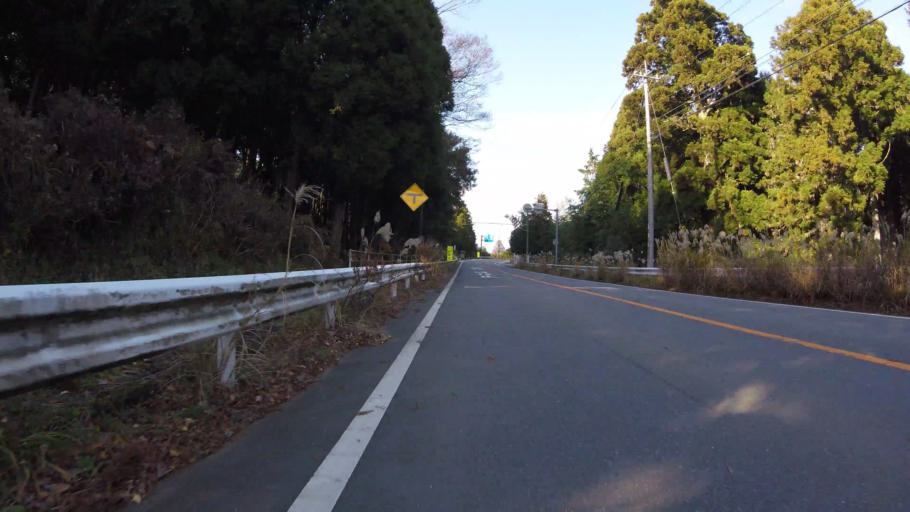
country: JP
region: Kanagawa
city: Hakone
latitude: 35.1571
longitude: 138.9957
